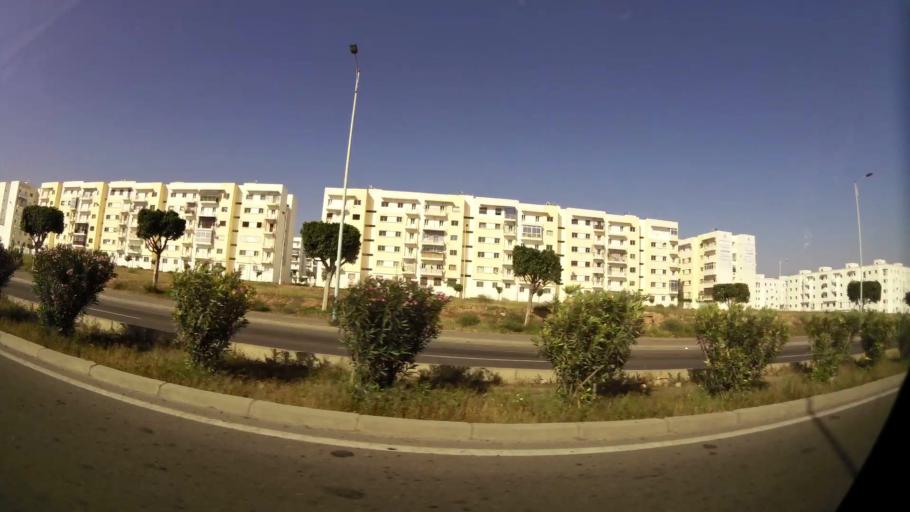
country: MA
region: Souss-Massa-Draa
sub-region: Inezgane-Ait Mellou
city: Inezgane
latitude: 30.3865
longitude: -9.5097
